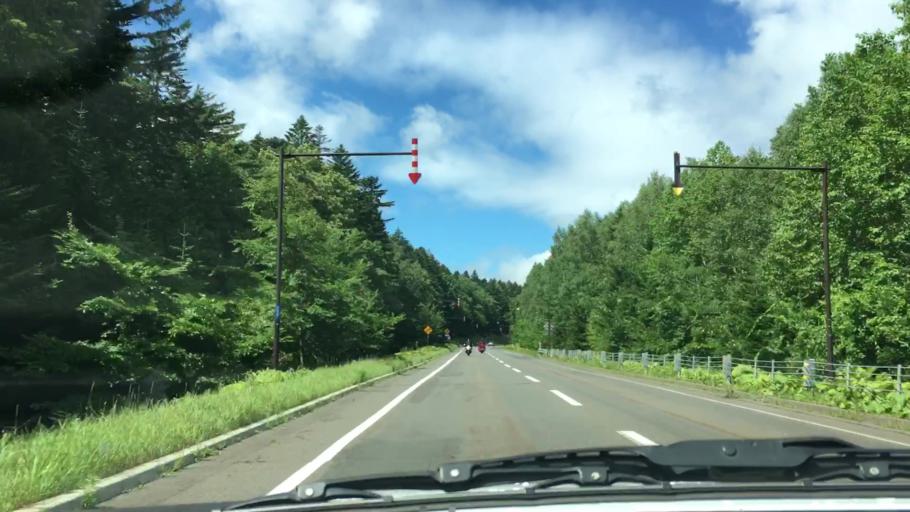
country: JP
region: Hokkaido
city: Bihoro
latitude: 43.4375
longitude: 144.0584
